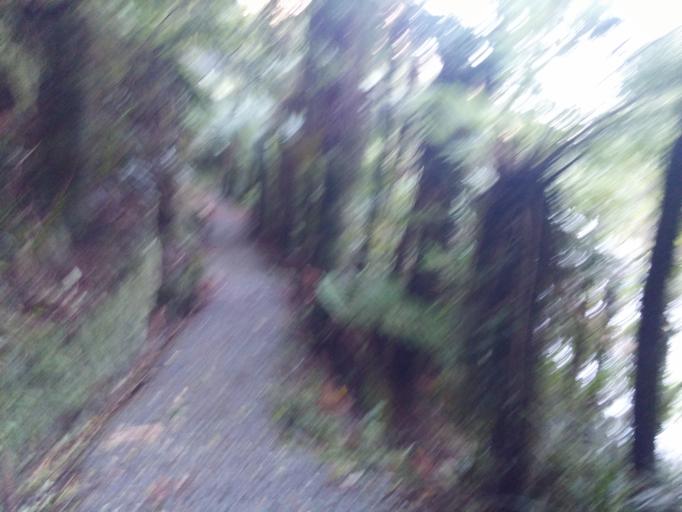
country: NZ
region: West Coast
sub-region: Grey District
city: Greymouth
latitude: -42.1168
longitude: 171.3633
